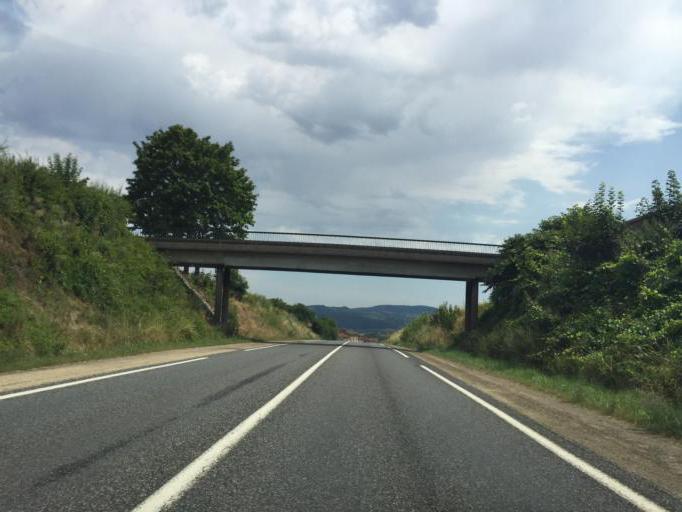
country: FR
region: Rhone-Alpes
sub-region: Departement du Rhone
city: Bully
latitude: 45.8526
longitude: 4.5784
